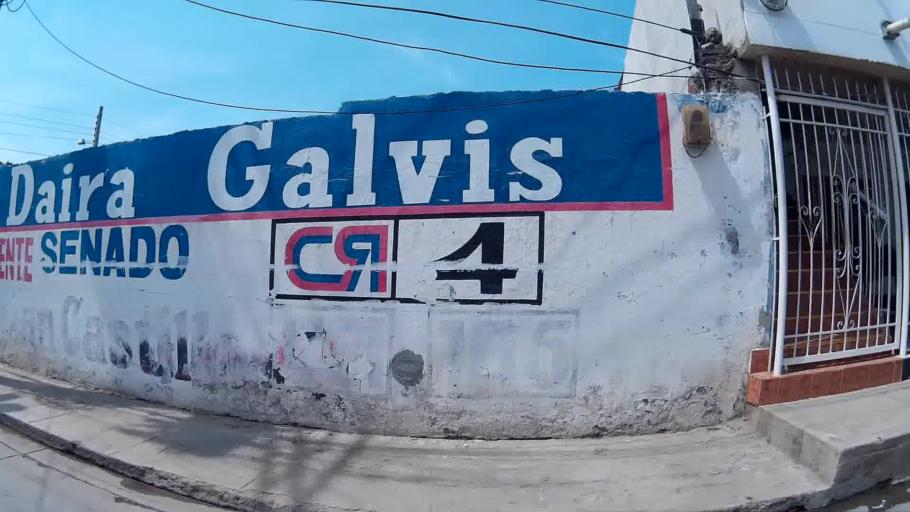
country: CO
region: Magdalena
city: Cienaga
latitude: 11.0133
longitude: -74.2482
